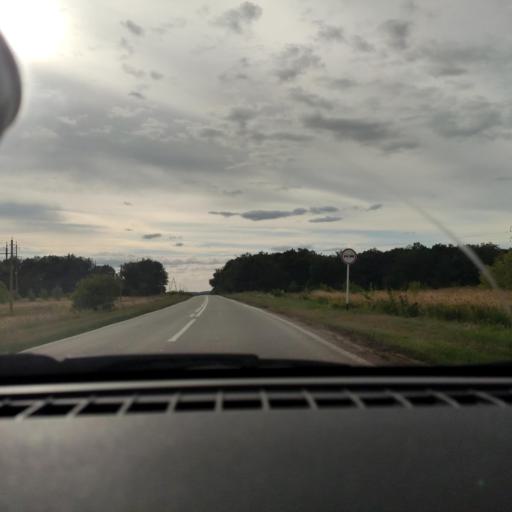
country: RU
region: Samara
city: Georgiyevka
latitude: 53.4275
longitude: 50.8053
